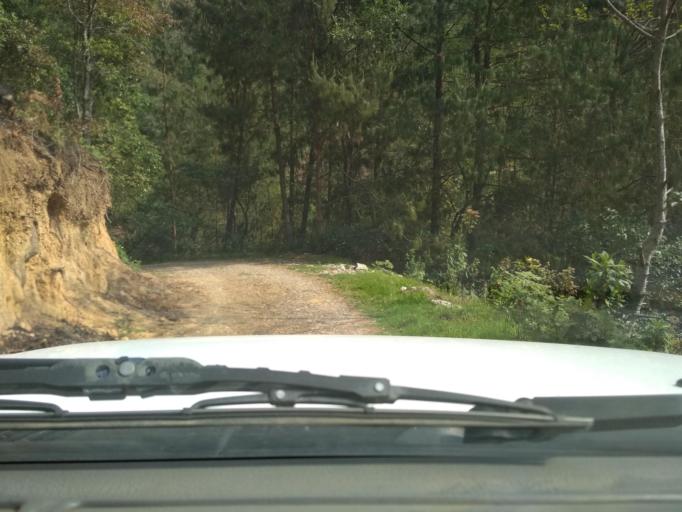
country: MX
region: Veracruz
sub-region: Soledad Atzompa
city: Tlatilpa
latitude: 18.7539
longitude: -97.1527
